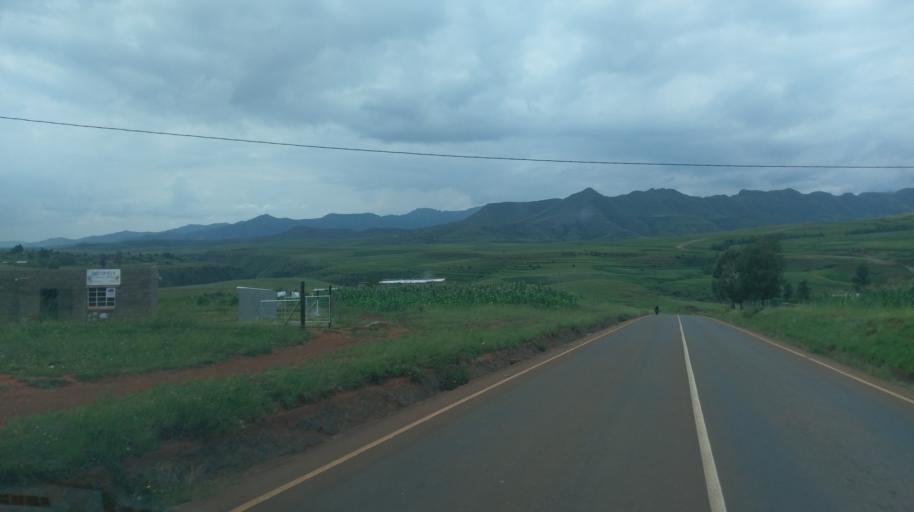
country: LS
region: Leribe
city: Leribe
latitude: -29.0394
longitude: 28.2445
